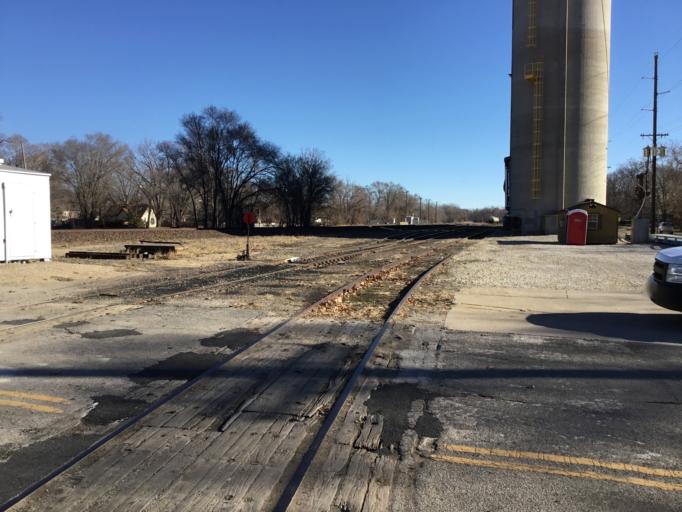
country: US
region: Kansas
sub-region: Douglas County
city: Lawrence
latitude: 38.9780
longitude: -95.2332
